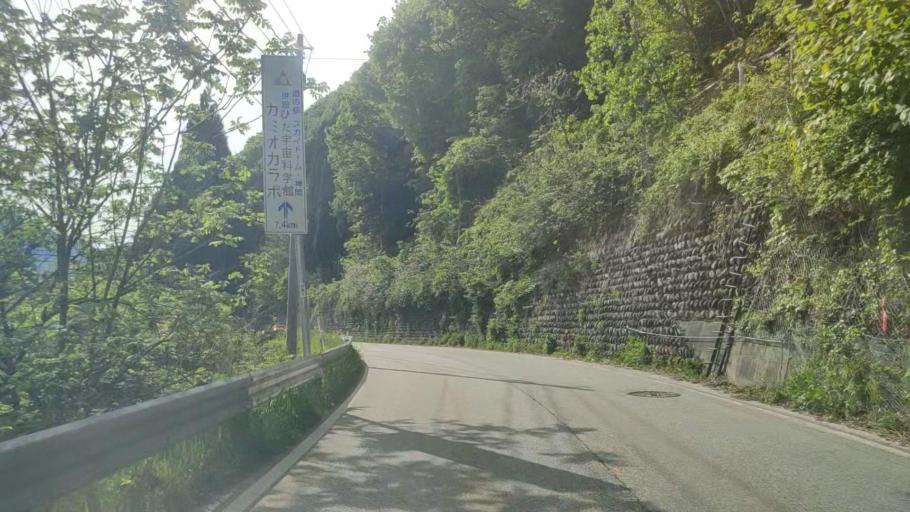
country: JP
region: Gifu
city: Takayama
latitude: 36.2970
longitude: 137.3649
